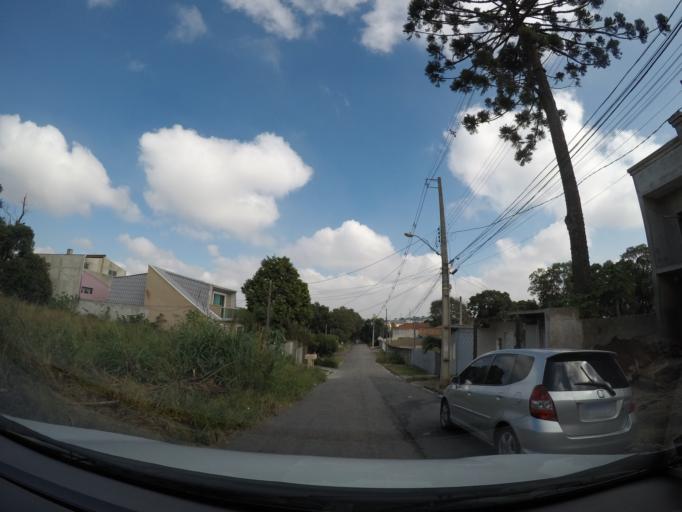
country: BR
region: Parana
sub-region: Sao Jose Dos Pinhais
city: Sao Jose dos Pinhais
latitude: -25.4918
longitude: -49.2170
